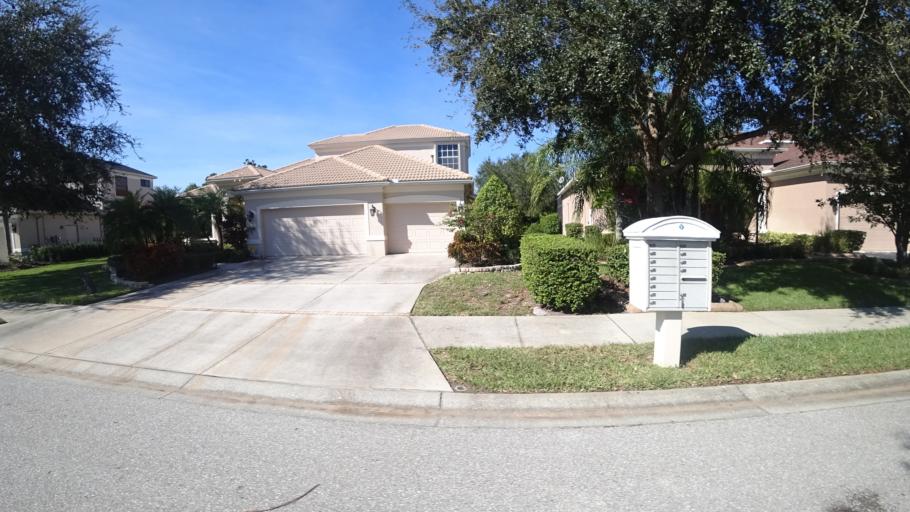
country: US
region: Florida
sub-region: Sarasota County
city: The Meadows
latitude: 27.4246
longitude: -82.4074
